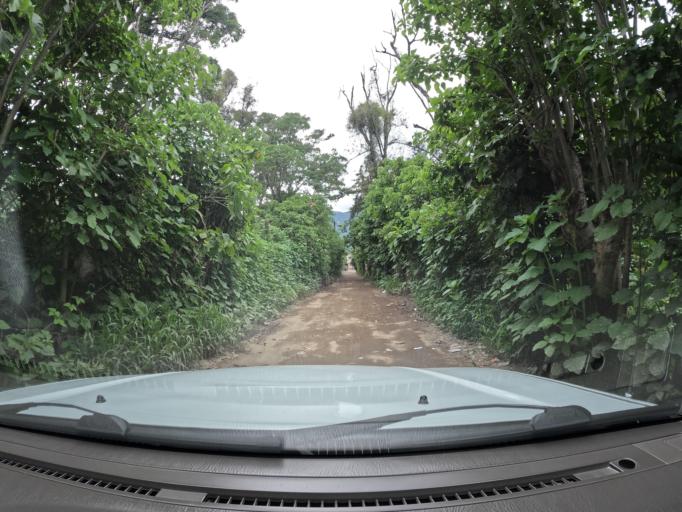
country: GT
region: Sacatepequez
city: Jocotenango
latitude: 14.5717
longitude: -90.7387
